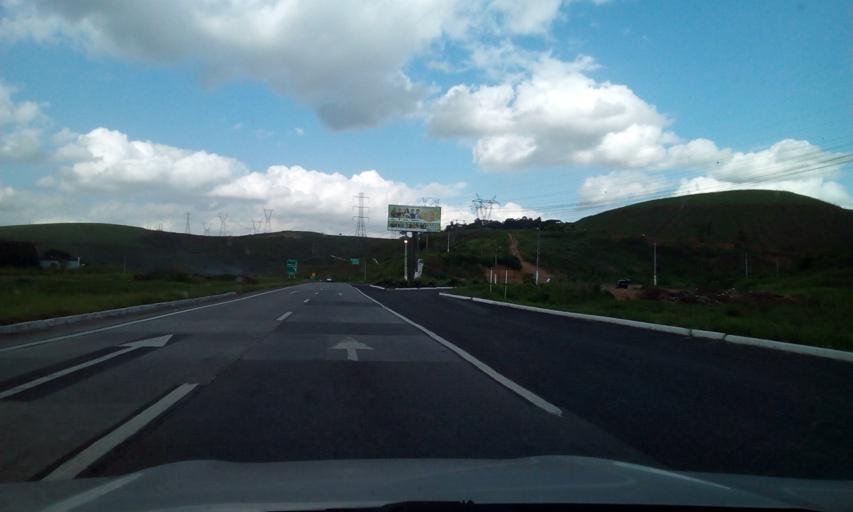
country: BR
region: Pernambuco
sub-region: Joaquim Nabuco
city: Joaquim Nabuco
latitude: -8.6215
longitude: -35.5511
